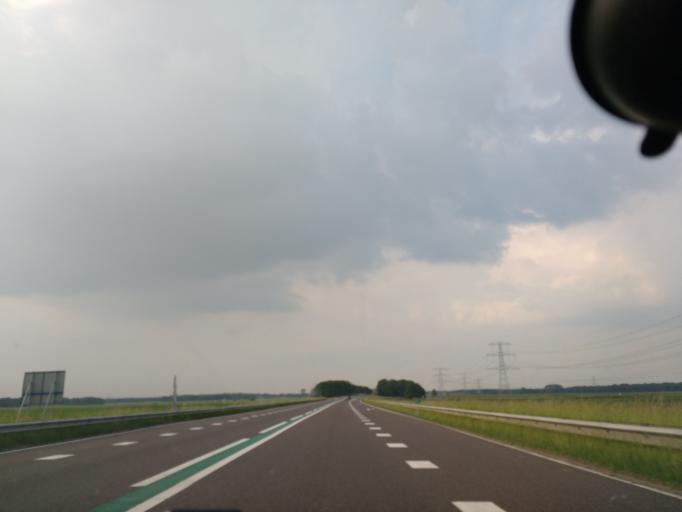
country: NL
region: Drenthe
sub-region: Gemeente Coevorden
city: Sleen
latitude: 52.7859
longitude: 6.8463
